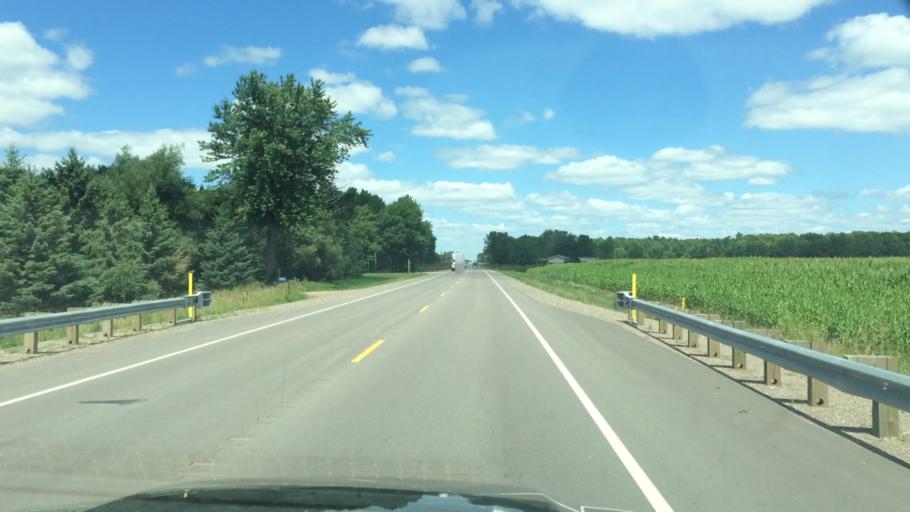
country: US
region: Wisconsin
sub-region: Clark County
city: Abbotsford
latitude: 45.0200
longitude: -90.3151
